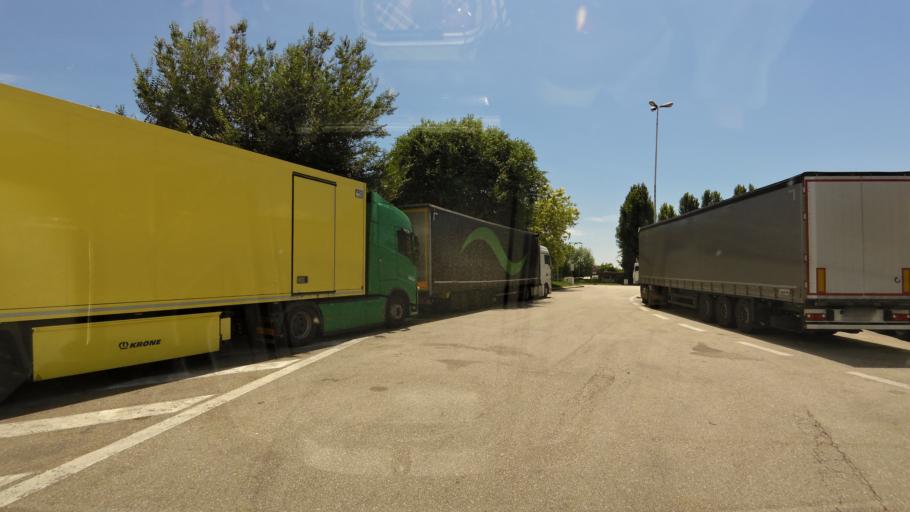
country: IT
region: Veneto
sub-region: Provincia di Venezia
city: Teglio Veneto
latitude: 45.8044
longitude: 12.8867
